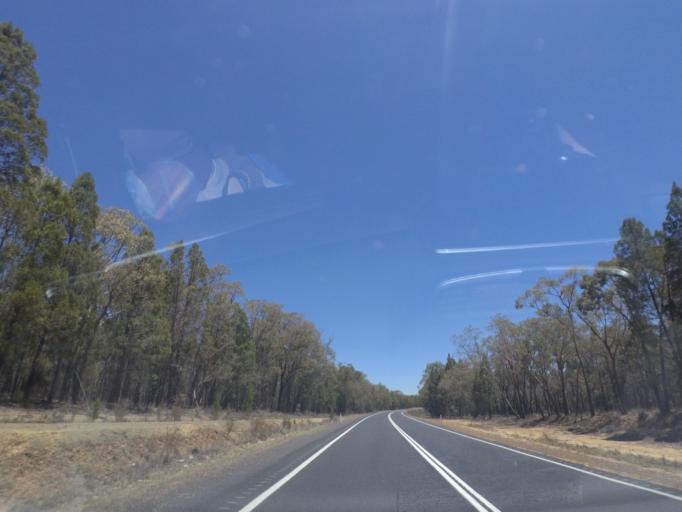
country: AU
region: New South Wales
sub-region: Warrumbungle Shire
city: Coonabarabran
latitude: -31.1941
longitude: 149.3520
